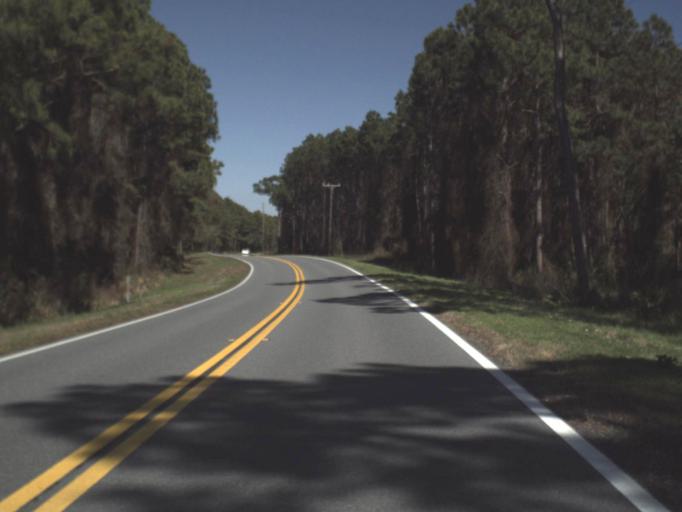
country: US
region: Florida
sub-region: Franklin County
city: Carrabelle
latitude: 29.9117
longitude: -84.5334
